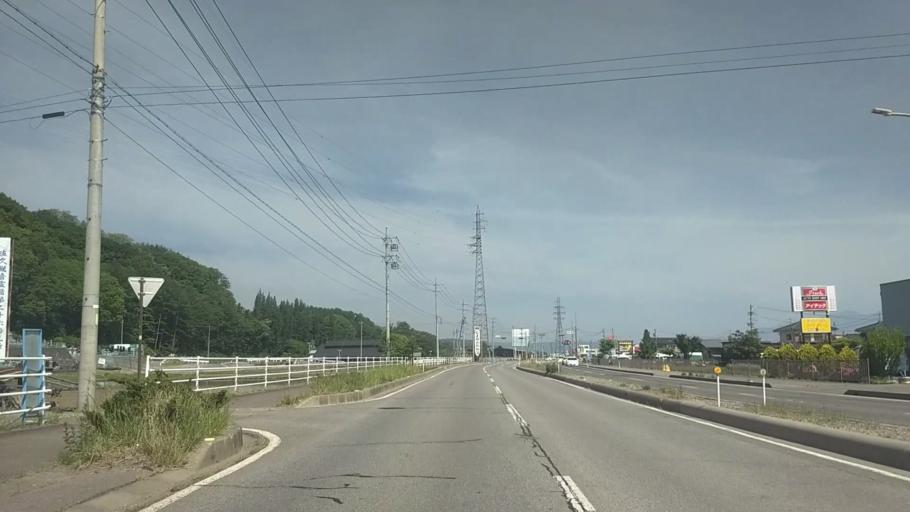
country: JP
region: Nagano
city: Saku
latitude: 36.1997
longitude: 138.4714
